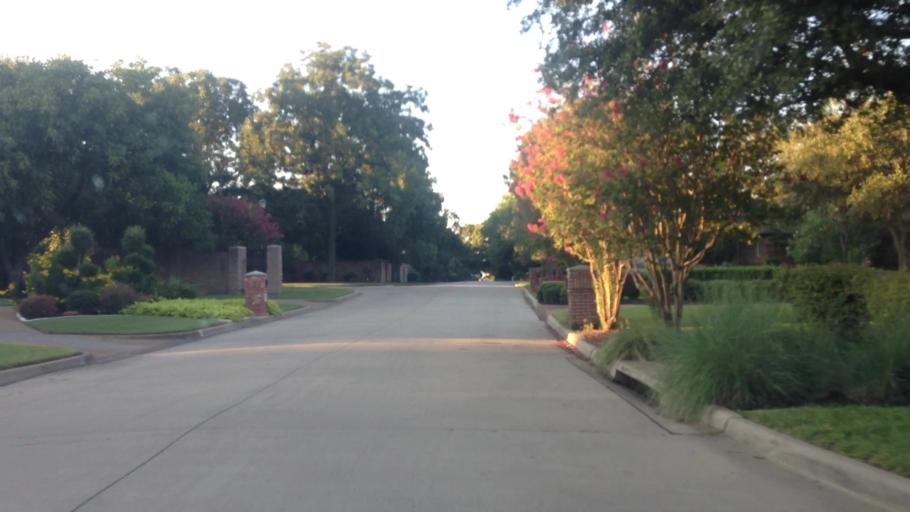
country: US
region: Texas
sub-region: Tarrant County
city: Southlake
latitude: 32.9315
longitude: -97.1284
